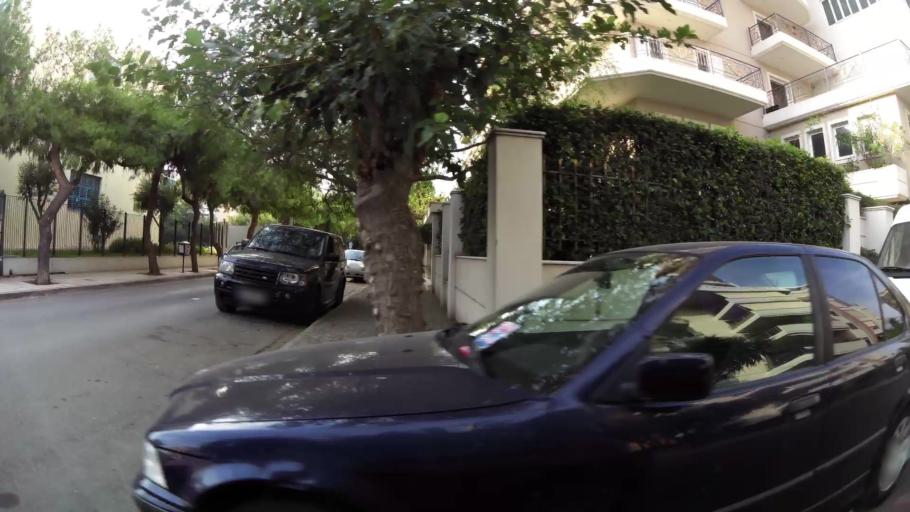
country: GR
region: Attica
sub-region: Nomarchia Athinas
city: Palaio Faliro
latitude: 37.9360
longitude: 23.6964
